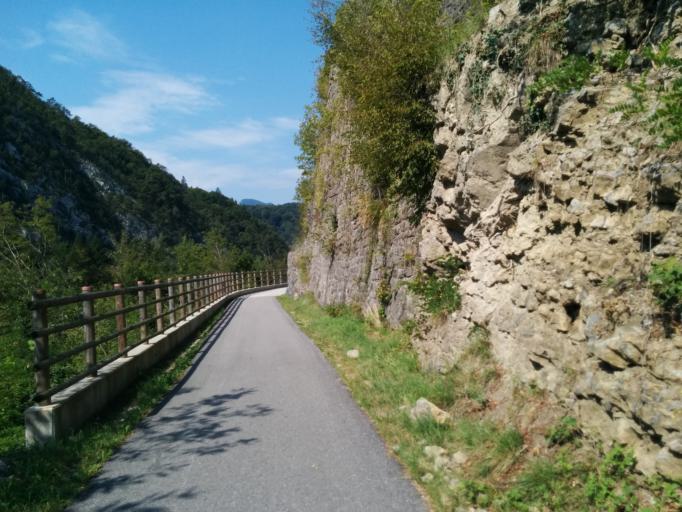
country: IT
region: Friuli Venezia Giulia
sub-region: Provincia di Udine
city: Raveo
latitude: 46.4293
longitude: 12.8989
